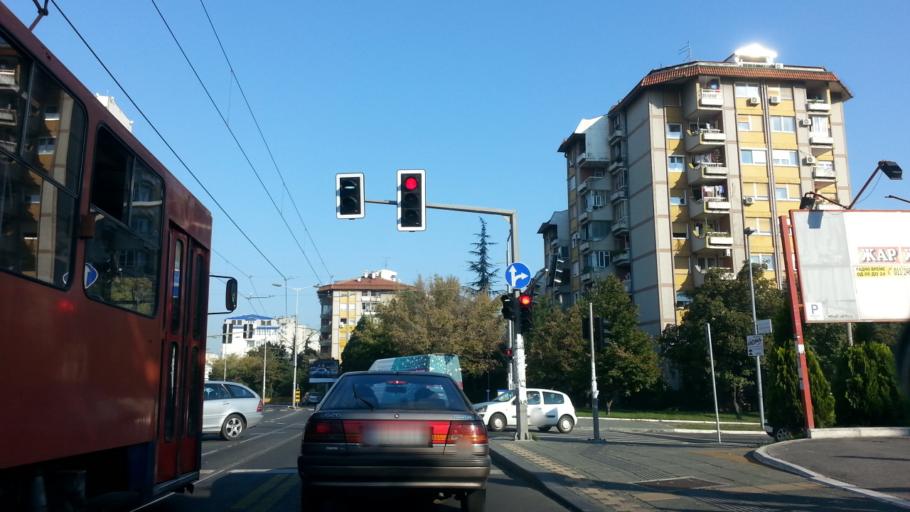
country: RS
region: Central Serbia
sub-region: Belgrade
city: Vozdovac
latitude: 44.7665
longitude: 20.4819
